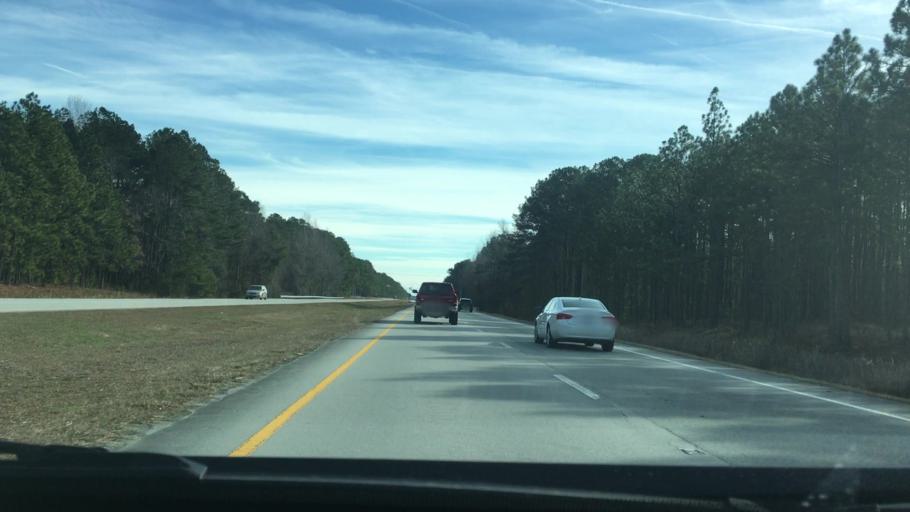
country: US
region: North Carolina
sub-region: Carteret County
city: Newport
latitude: 34.7737
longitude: -76.8691
